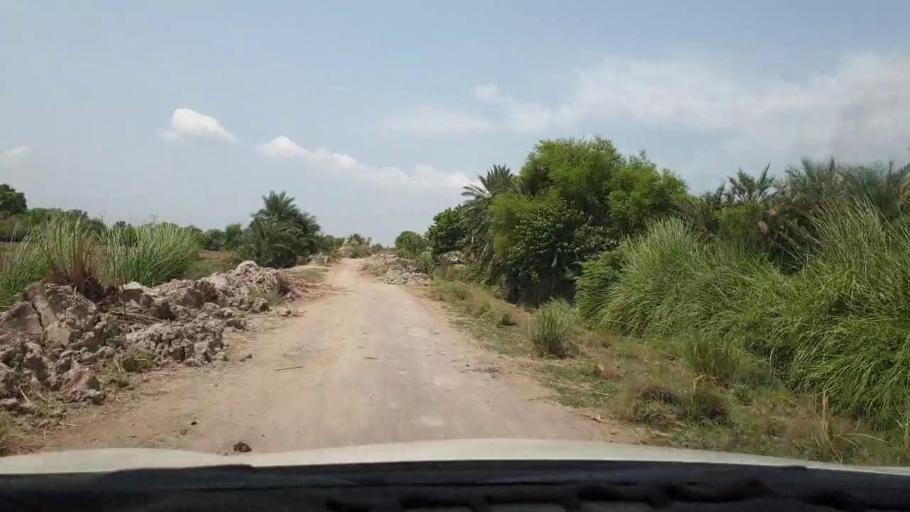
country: PK
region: Sindh
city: Ratodero
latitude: 27.8360
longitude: 68.2161
